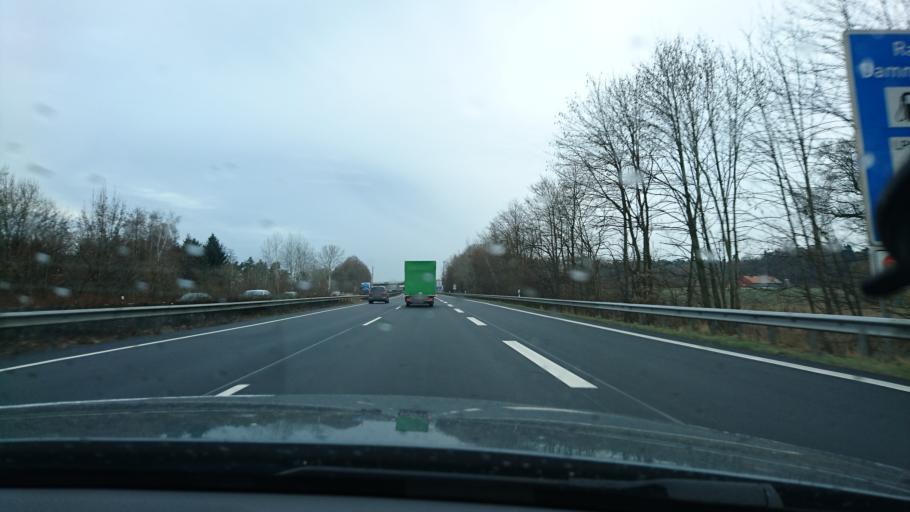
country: DE
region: Lower Saxony
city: Holdorf
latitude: 52.5330
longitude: 8.1122
